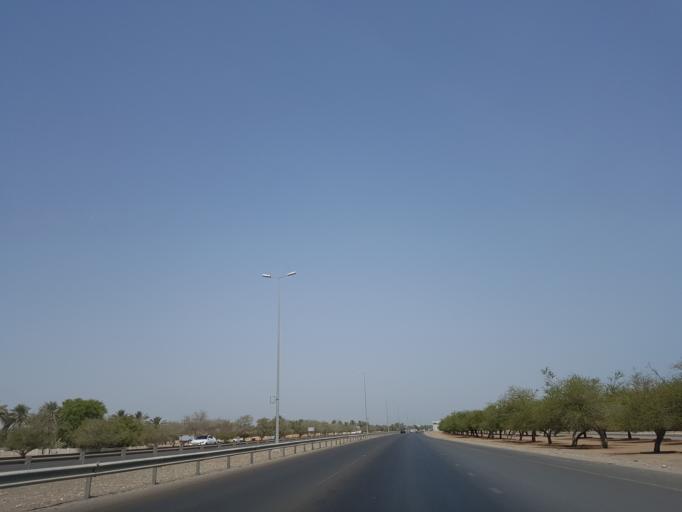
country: OM
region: Al Batinah
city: Saham
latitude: 24.0867
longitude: 56.9328
